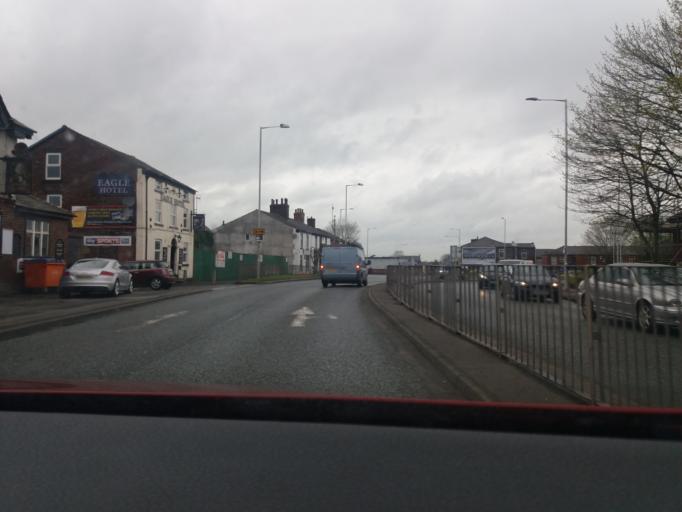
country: GB
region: England
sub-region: Lancashire
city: Chorley
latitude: 53.6472
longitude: -2.6273
